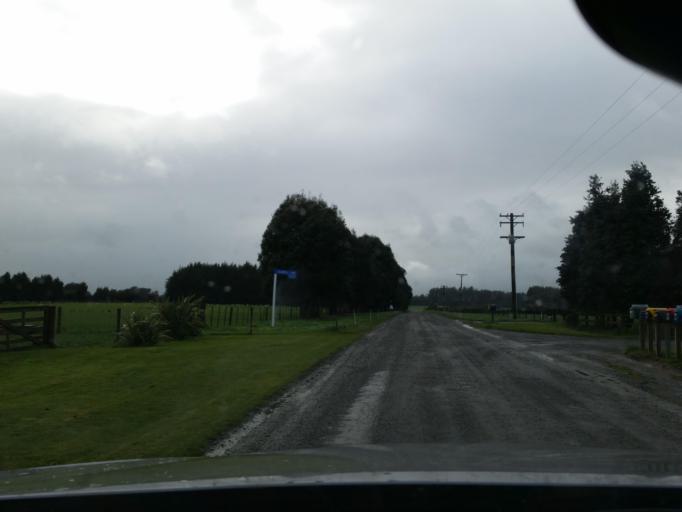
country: NZ
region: Southland
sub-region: Invercargill City
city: Invercargill
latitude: -46.3557
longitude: 168.4442
